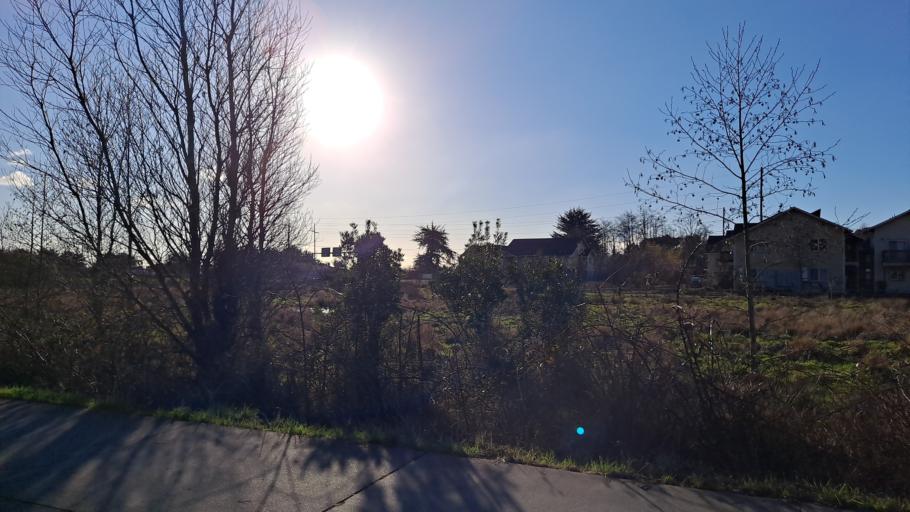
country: US
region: California
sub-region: Humboldt County
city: Arcata
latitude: 40.8627
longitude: -124.0771
